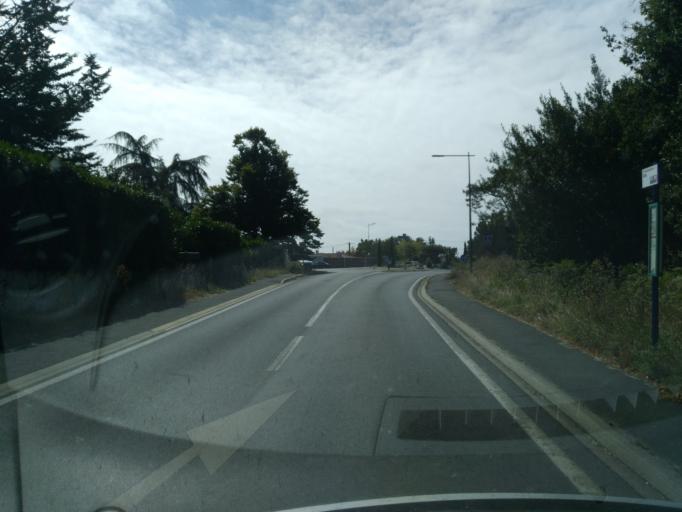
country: FR
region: Poitou-Charentes
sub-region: Departement de la Charente-Maritime
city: Vaux-sur-Mer
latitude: 45.6643
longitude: -1.0725
